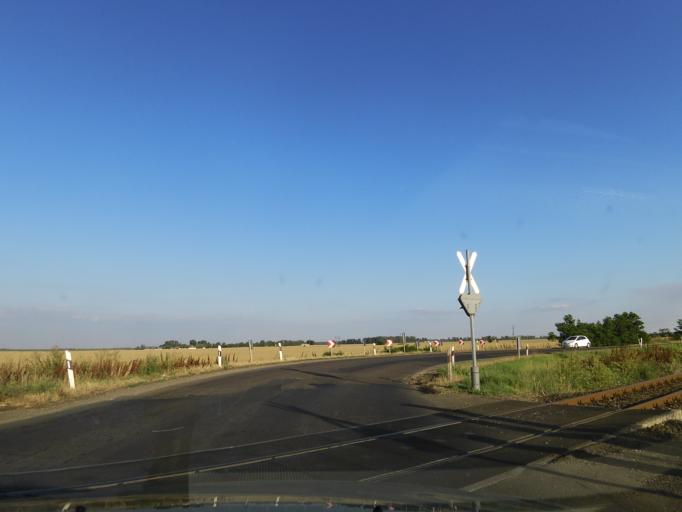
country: HU
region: Jasz-Nagykun-Szolnok
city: Tiszafoldvar
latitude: 46.9584
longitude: 20.2727
